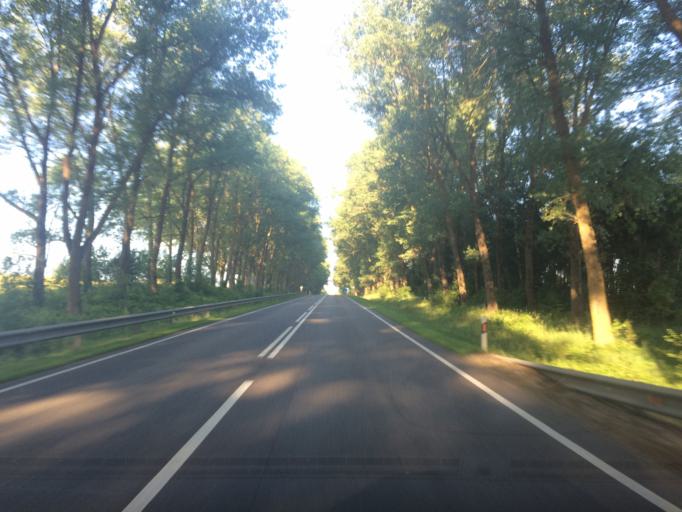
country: LT
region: Utenos apskritis
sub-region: Anyksciai
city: Anyksciai
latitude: 55.3968
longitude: 25.0833
